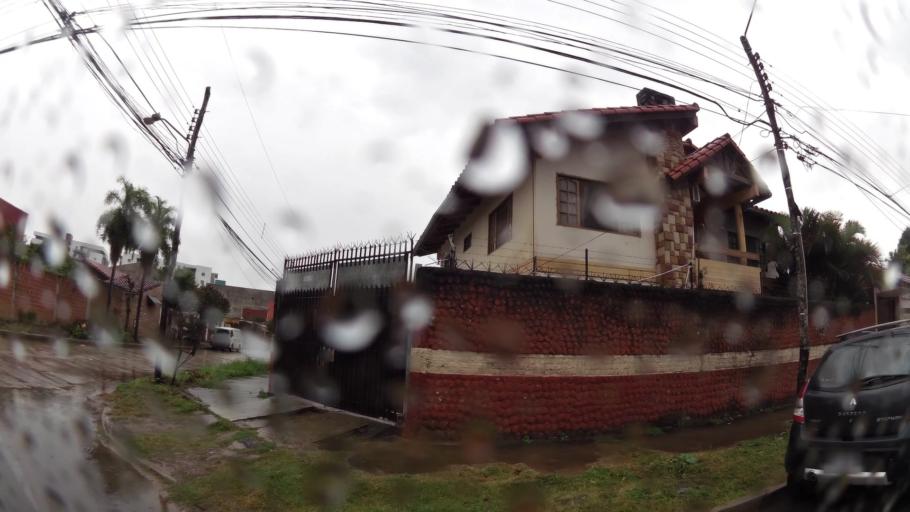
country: BO
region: Santa Cruz
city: Santa Cruz de la Sierra
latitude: -17.7935
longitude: -63.2196
